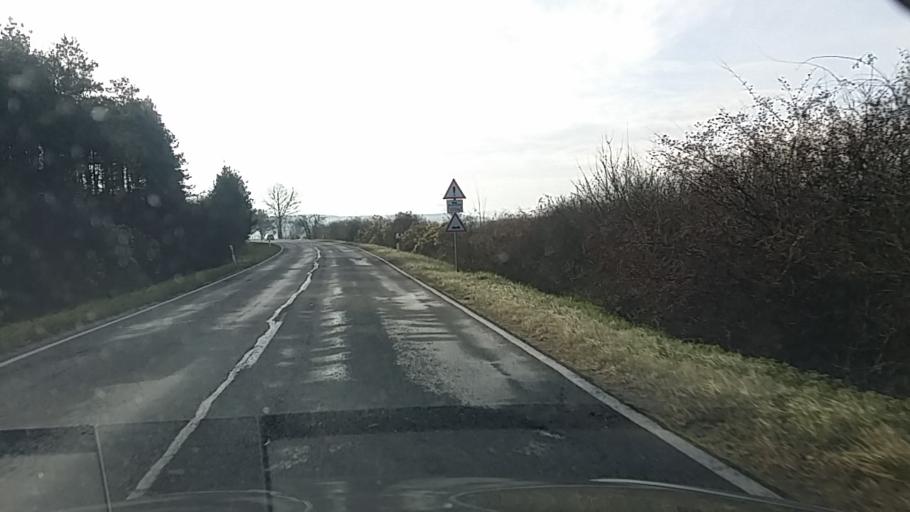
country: HU
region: Veszprem
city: Urkut
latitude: 46.9801
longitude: 17.6273
